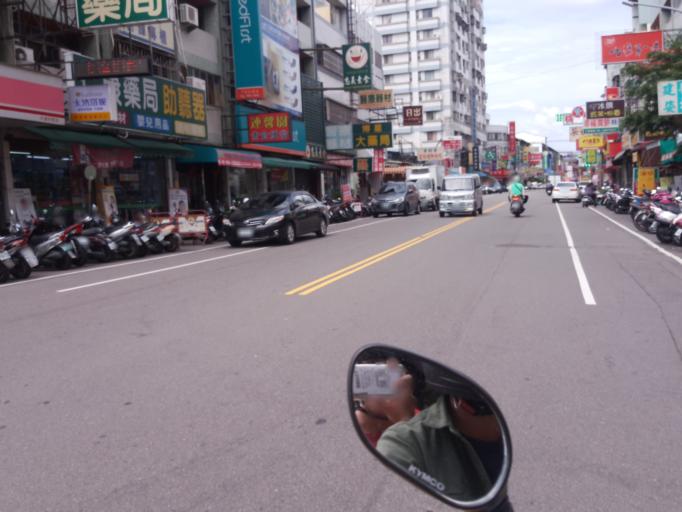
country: TW
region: Taiwan
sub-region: Taichung City
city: Taichung
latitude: 24.1095
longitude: 120.6806
